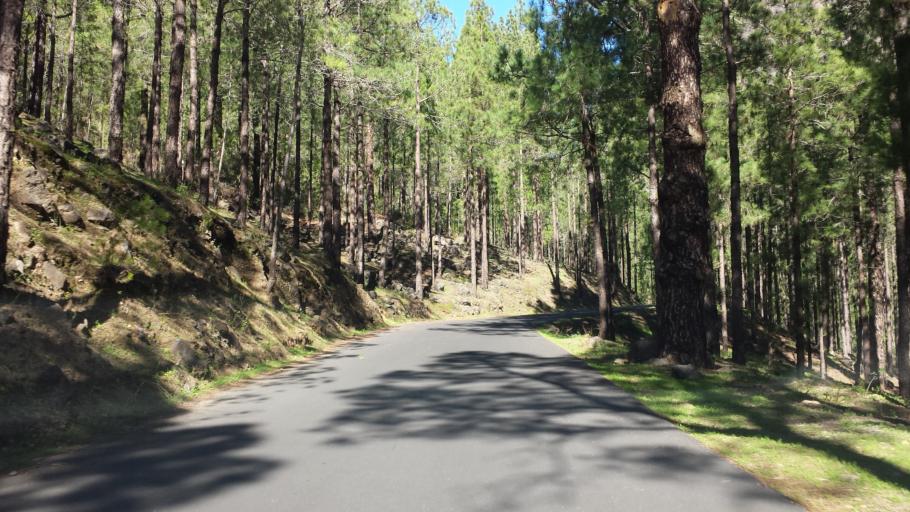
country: ES
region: Canary Islands
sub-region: Provincia de Santa Cruz de Tenerife
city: El Paso
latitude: 28.6841
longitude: -17.8482
